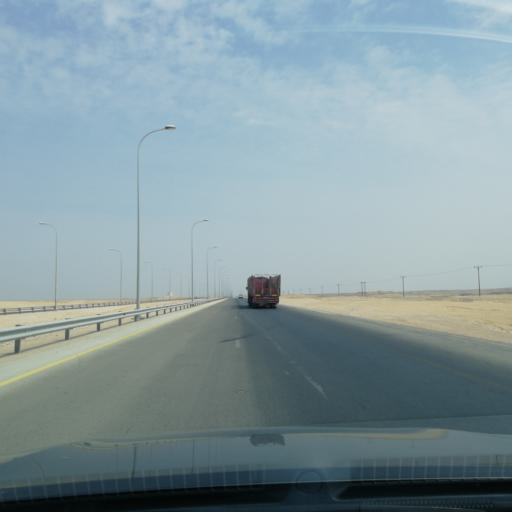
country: OM
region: Zufar
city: Salalah
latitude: 17.6725
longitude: 54.0560
